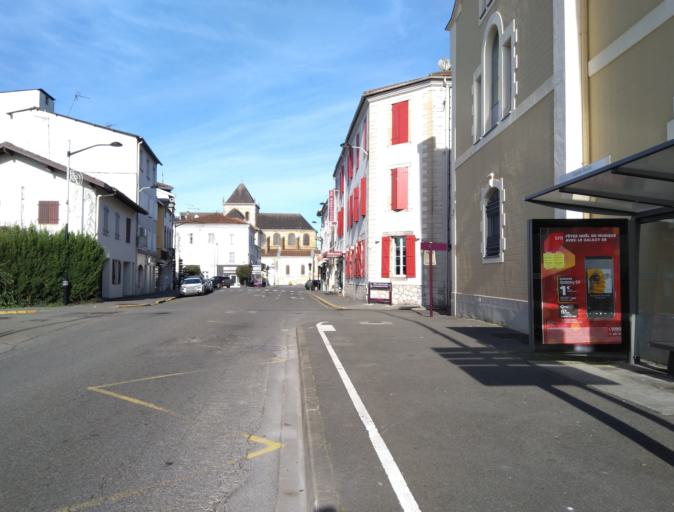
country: FR
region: Aquitaine
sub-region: Departement des Landes
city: Dax
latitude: 43.7066
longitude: -1.0526
